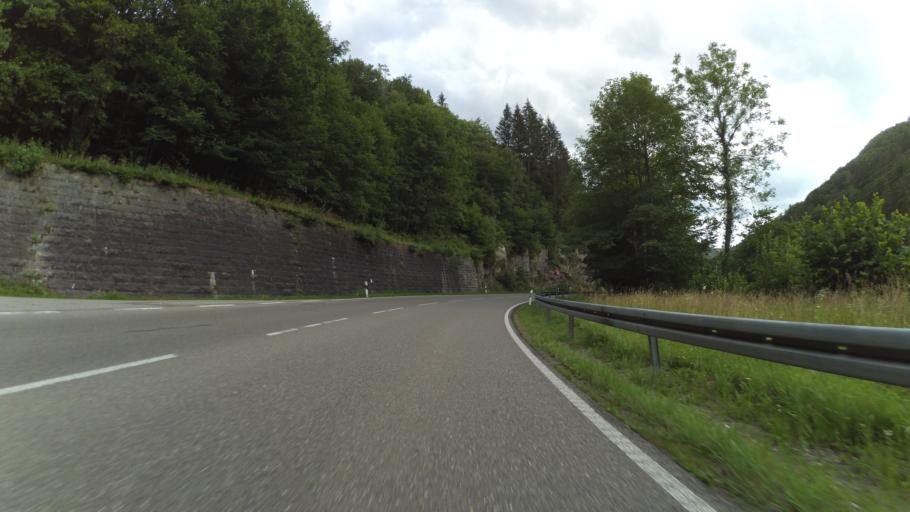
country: DE
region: Baden-Wuerttemberg
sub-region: Freiburg Region
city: Todtnau
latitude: 47.8125
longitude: 7.9379
